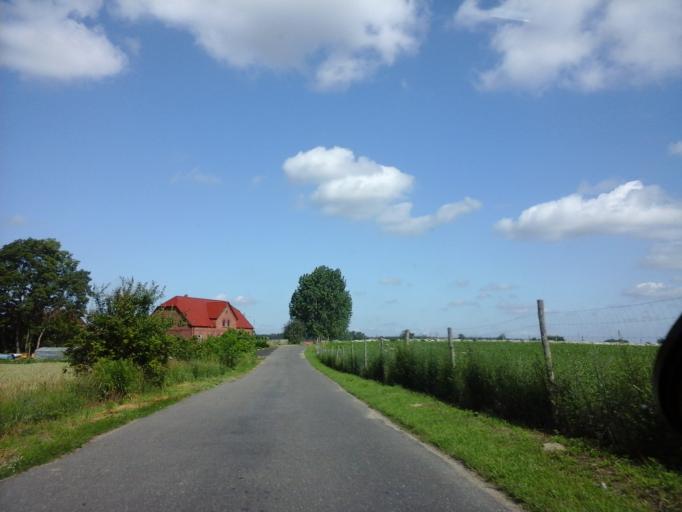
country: PL
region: West Pomeranian Voivodeship
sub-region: Powiat choszczenski
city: Recz
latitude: 53.2067
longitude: 15.5530
